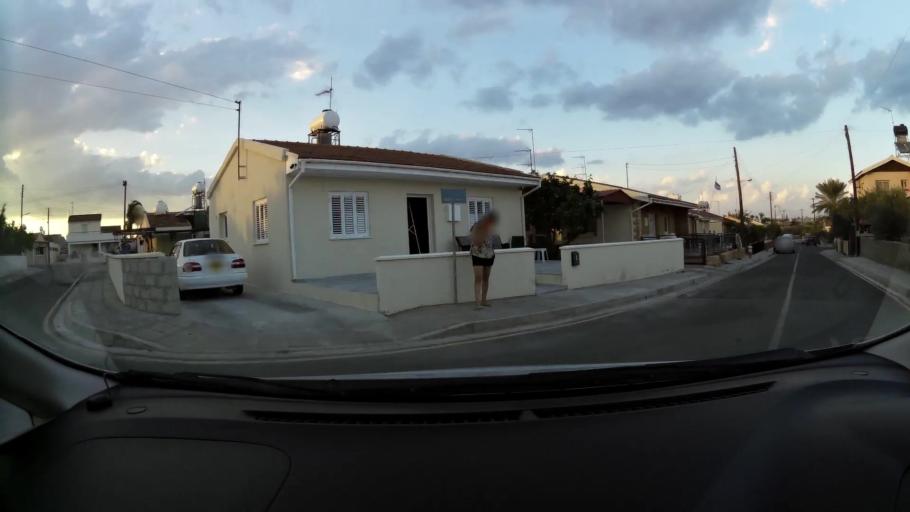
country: CY
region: Larnaka
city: Meneou
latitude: 34.8671
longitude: 33.5900
